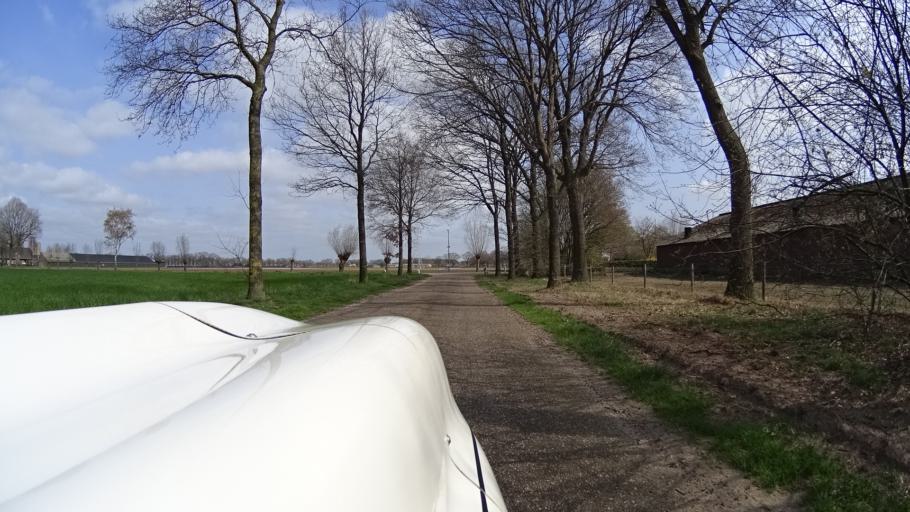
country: NL
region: North Brabant
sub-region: Gemeente Boekel
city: Boekel
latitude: 51.5960
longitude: 5.6470
